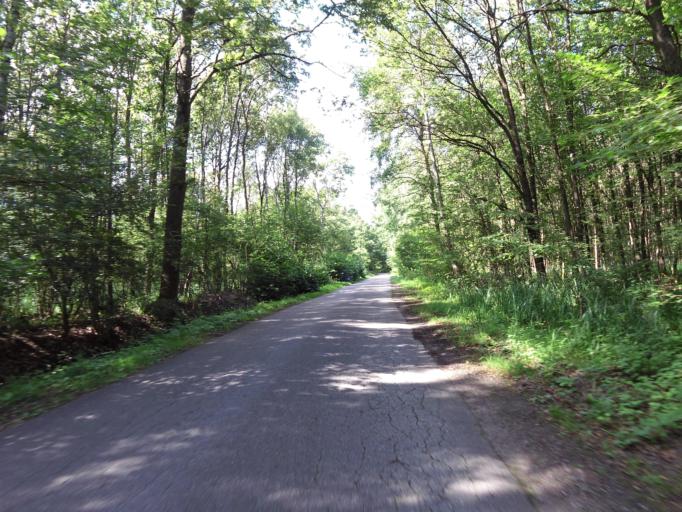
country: DE
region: Rheinland-Pfalz
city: Hanhofen
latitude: 49.3432
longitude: 8.3281
